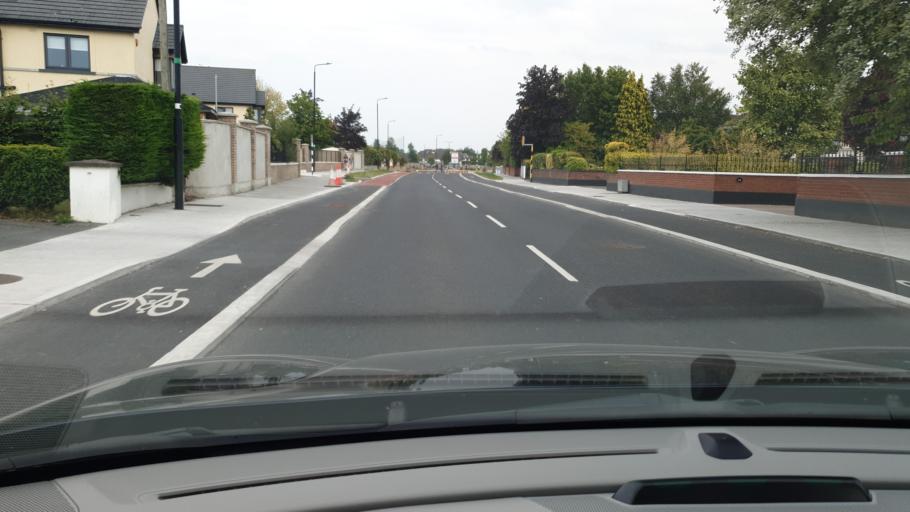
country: IE
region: Leinster
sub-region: An Mhi
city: Ashbourne
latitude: 53.5091
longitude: -6.3917
